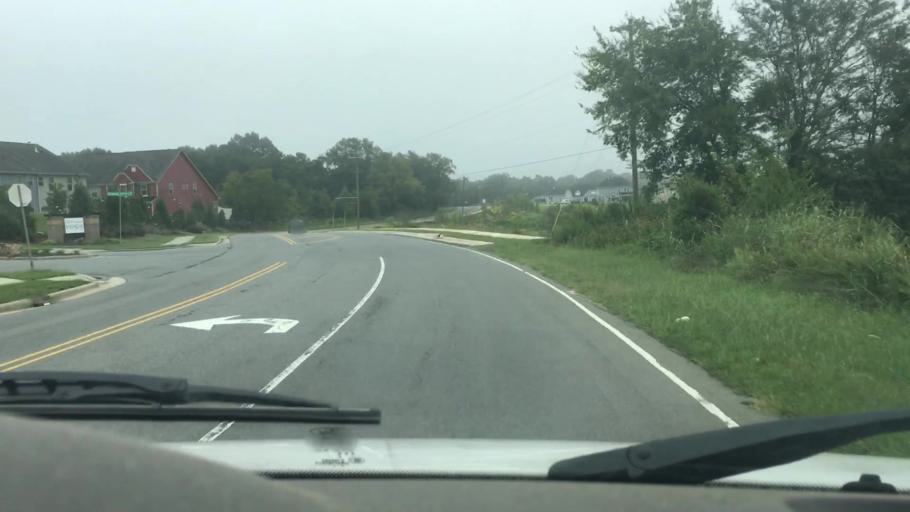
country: US
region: North Carolina
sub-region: Mecklenburg County
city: Huntersville
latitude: 35.4006
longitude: -80.7599
